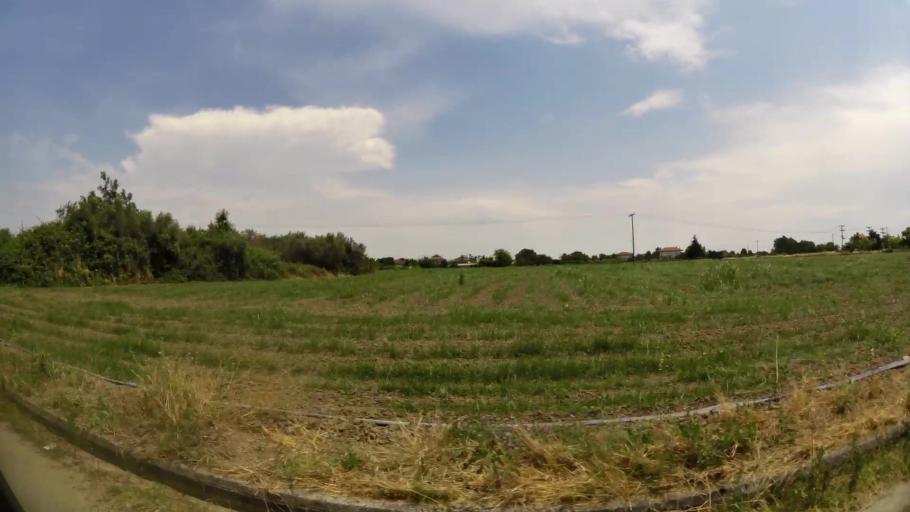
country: GR
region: Central Macedonia
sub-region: Nomos Pierias
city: Peristasi
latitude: 40.2662
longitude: 22.5346
